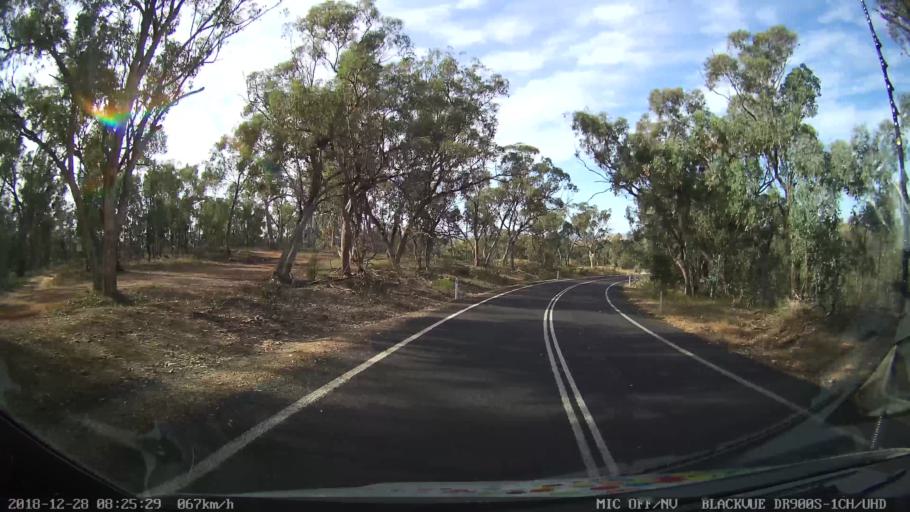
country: AU
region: New South Wales
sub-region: Blayney
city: Blayney
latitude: -33.9267
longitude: 149.3523
